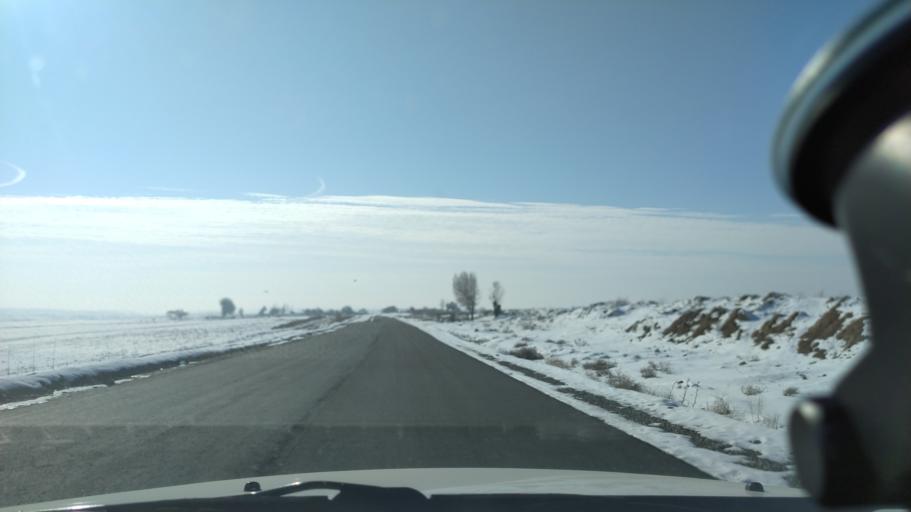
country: UZ
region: Namangan
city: Yangiqo`rg`on
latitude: 41.1516
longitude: 71.6577
